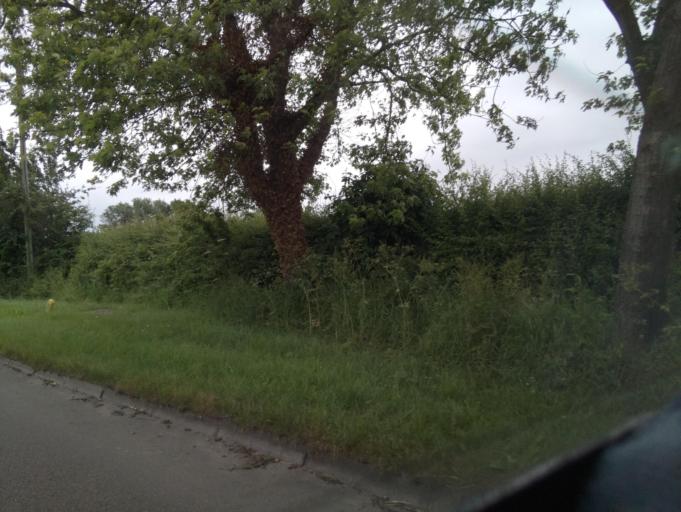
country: GB
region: England
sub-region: Leicestershire
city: Melton Mowbray
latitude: 52.7455
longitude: -0.8656
